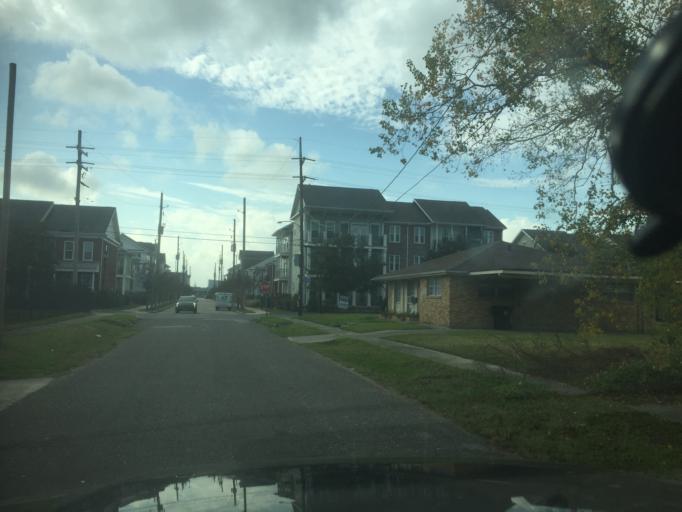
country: US
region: Louisiana
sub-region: Orleans Parish
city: New Orleans
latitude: 29.9970
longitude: -90.0743
